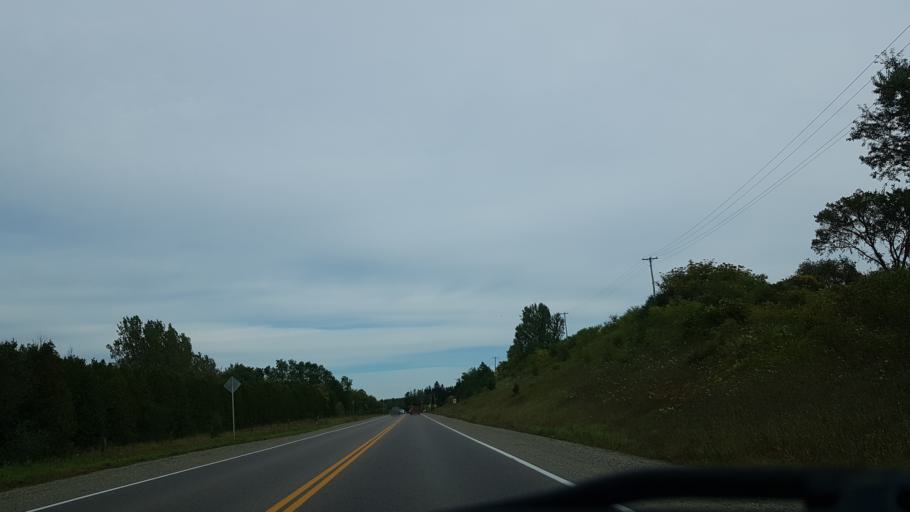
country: CA
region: Ontario
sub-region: Wellington County
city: Guelph
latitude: 43.6044
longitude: -80.2290
